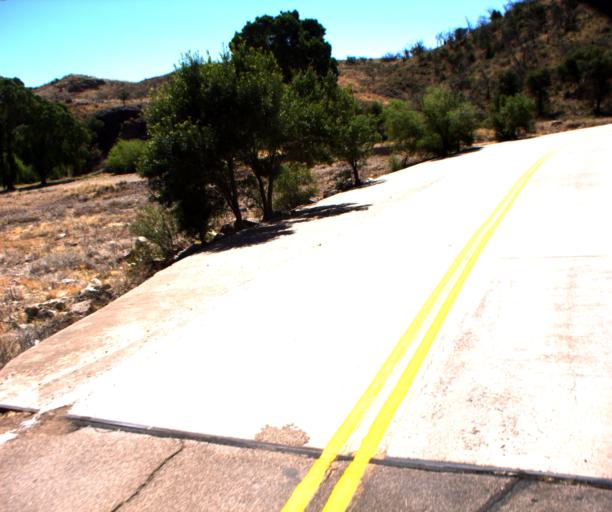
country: US
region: Arizona
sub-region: Santa Cruz County
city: Rio Rico
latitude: 31.3984
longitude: -111.0904
